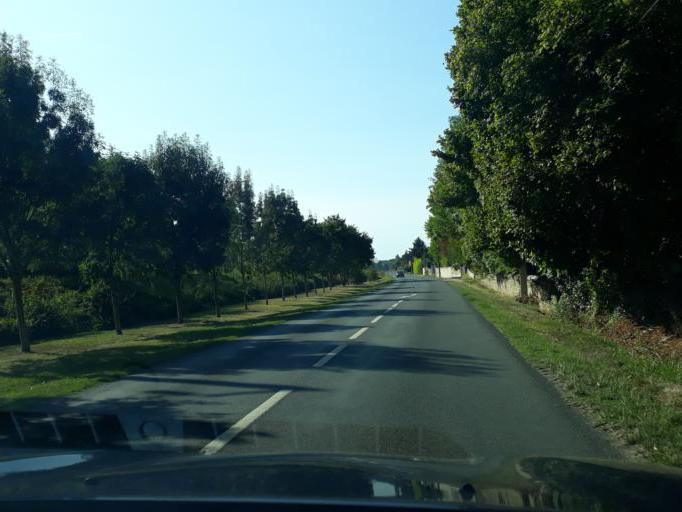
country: FR
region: Centre
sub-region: Departement du Loir-et-Cher
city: Thesee
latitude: 47.3277
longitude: 1.2987
